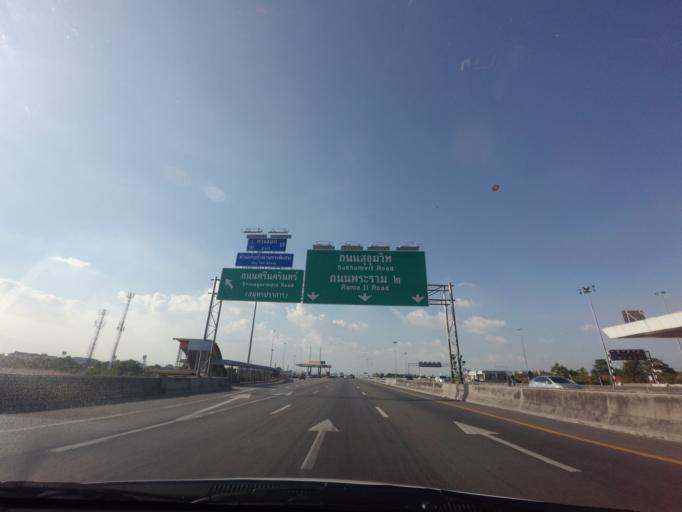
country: TH
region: Samut Prakan
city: Samut Prakan
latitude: 13.6082
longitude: 100.6248
